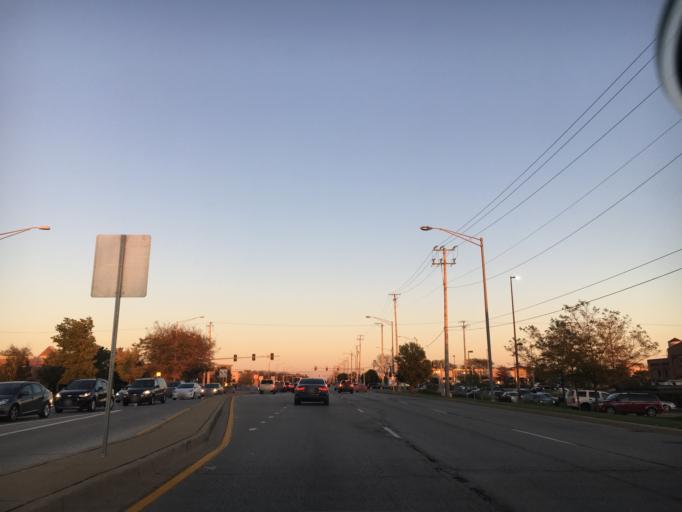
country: US
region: Illinois
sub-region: Cook County
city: Tinley Park
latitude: 41.6022
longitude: -87.7959
